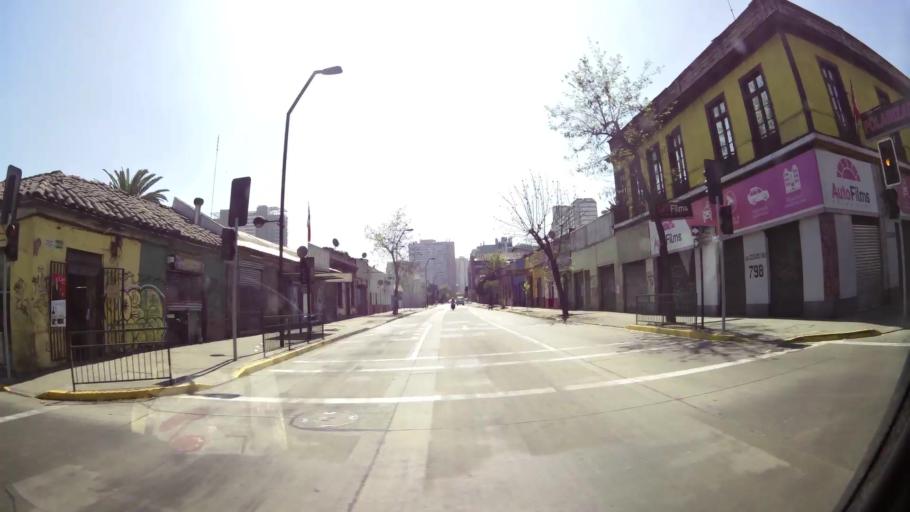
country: CL
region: Santiago Metropolitan
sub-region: Provincia de Santiago
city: Santiago
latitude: -33.4548
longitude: -70.6461
